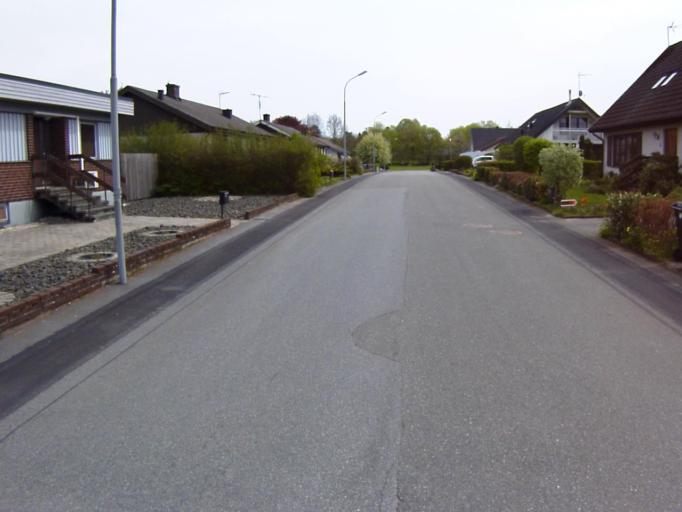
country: SE
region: Skane
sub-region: Kristianstads Kommun
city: Onnestad
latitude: 55.9369
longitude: 13.9865
